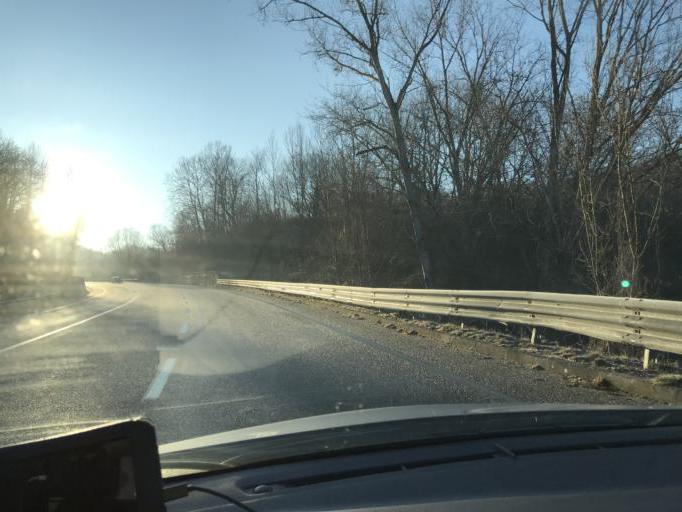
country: IT
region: Latium
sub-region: Provincia di Rieti
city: Concerviano
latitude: 42.3189
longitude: 13.0242
